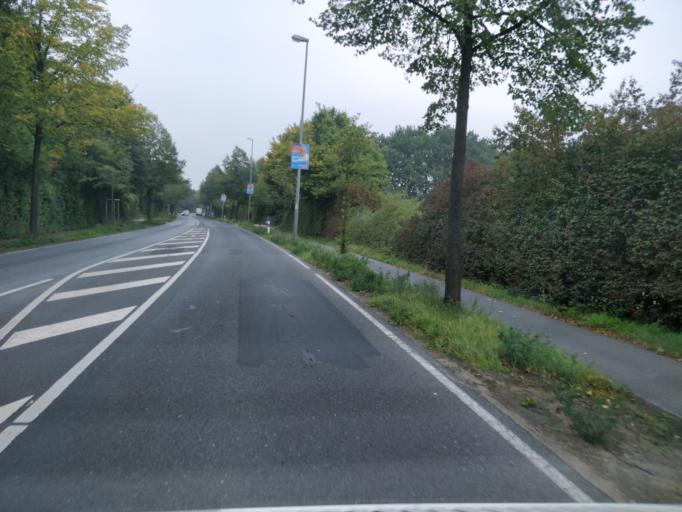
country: DE
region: North Rhine-Westphalia
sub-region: Regierungsbezirk Dusseldorf
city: Dinslaken
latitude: 51.5522
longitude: 6.7529
